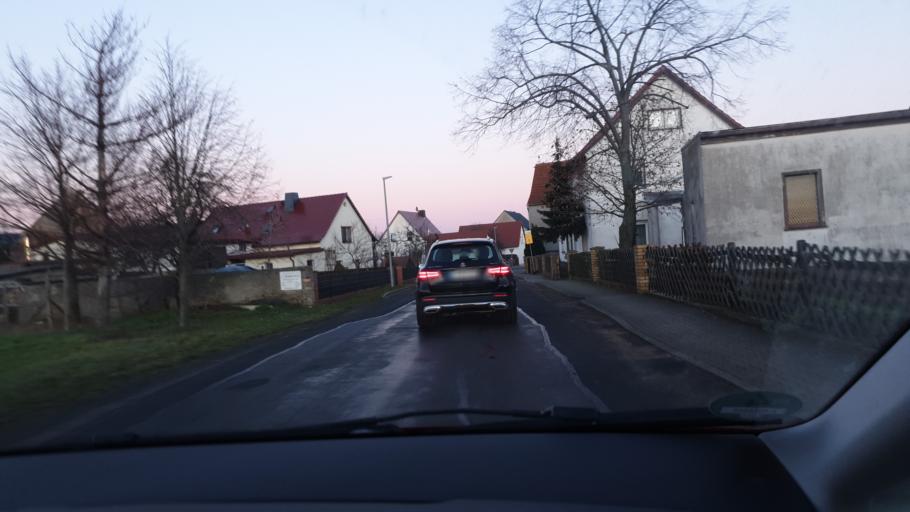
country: DE
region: Saxony
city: Mockrehna
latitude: 51.4707
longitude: 12.8034
